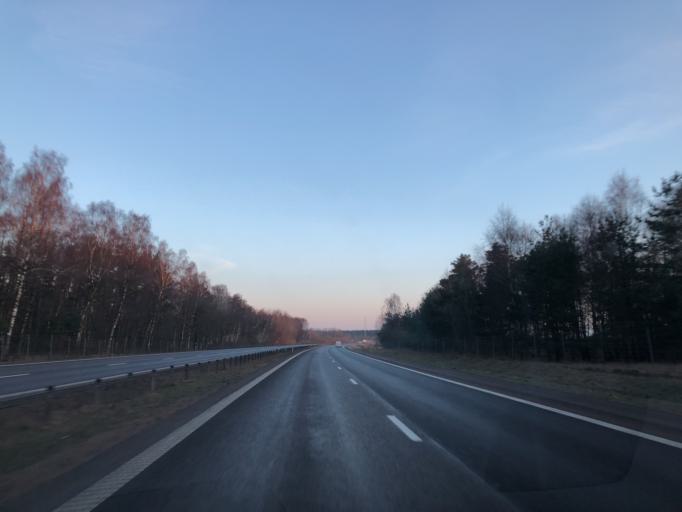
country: SE
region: Halland
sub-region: Laholms Kommun
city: Mellbystrand
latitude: 56.4661
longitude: 12.9414
